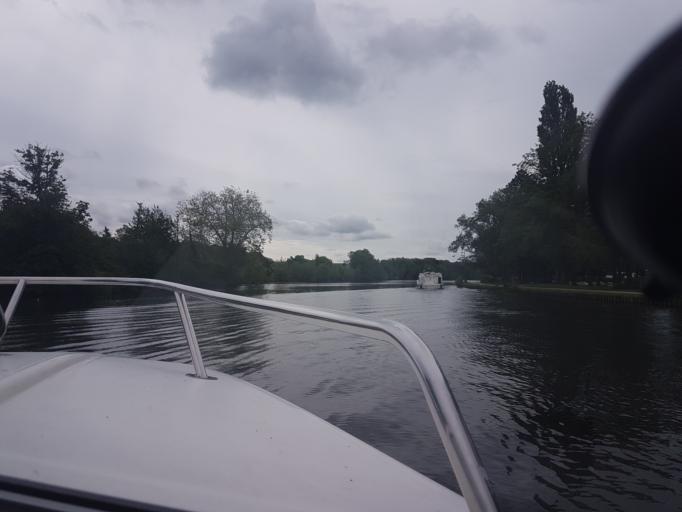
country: FR
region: Bourgogne
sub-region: Departement de l'Yonne
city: Auxerre
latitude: 47.7922
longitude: 3.5854
